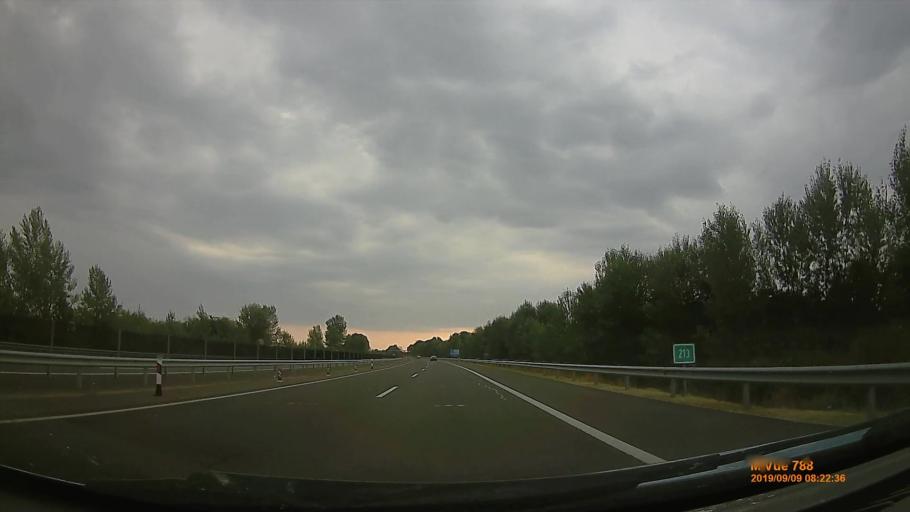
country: HU
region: Szabolcs-Szatmar-Bereg
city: Kalmanhaza
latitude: 47.8987
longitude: 21.5412
